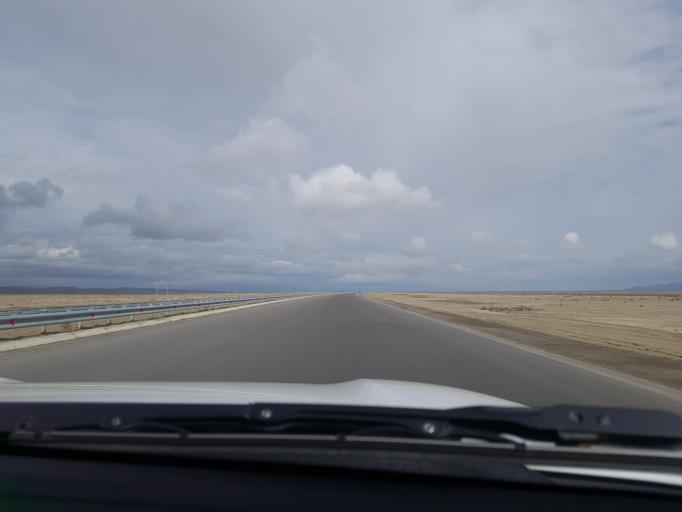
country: TM
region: Balkan
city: Gumdag
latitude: 39.2085
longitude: 55.0234
